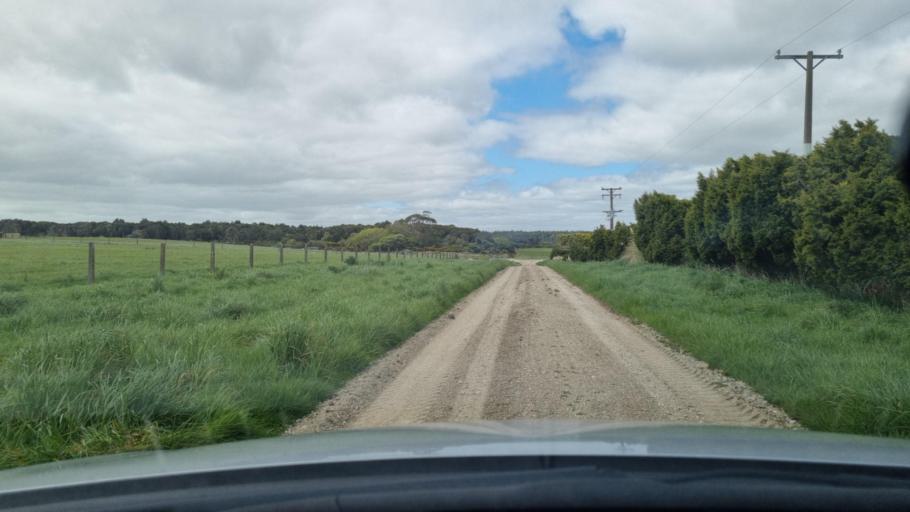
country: NZ
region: Southland
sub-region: Invercargill City
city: Invercargill
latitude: -46.4342
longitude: 168.4115
